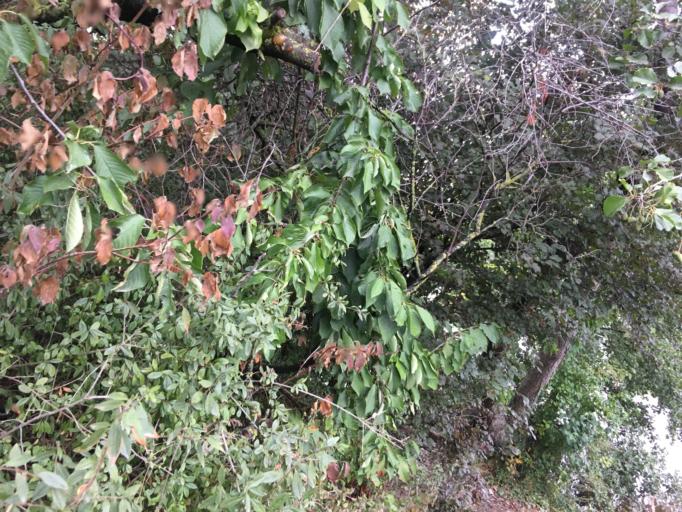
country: DE
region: Baden-Wuerttemberg
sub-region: Regierungsbezirk Stuttgart
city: Neckarsulm
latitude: 49.1825
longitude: 9.2134
